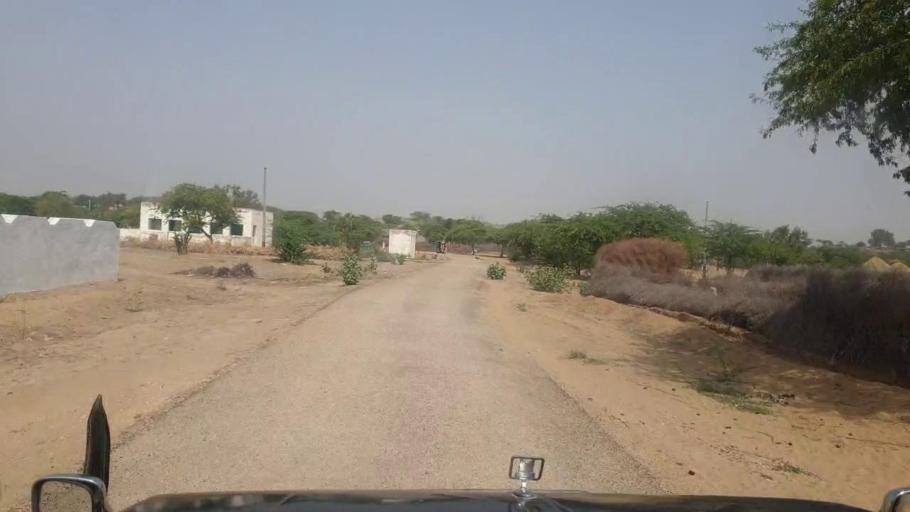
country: PK
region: Sindh
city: Islamkot
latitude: 25.0780
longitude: 70.1506
